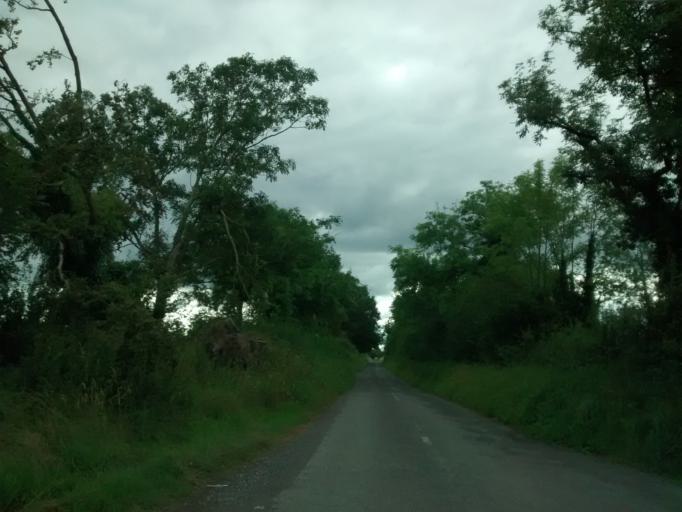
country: IE
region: Leinster
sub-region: Uibh Fhaili
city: Clara
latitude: 53.3680
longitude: -7.6271
